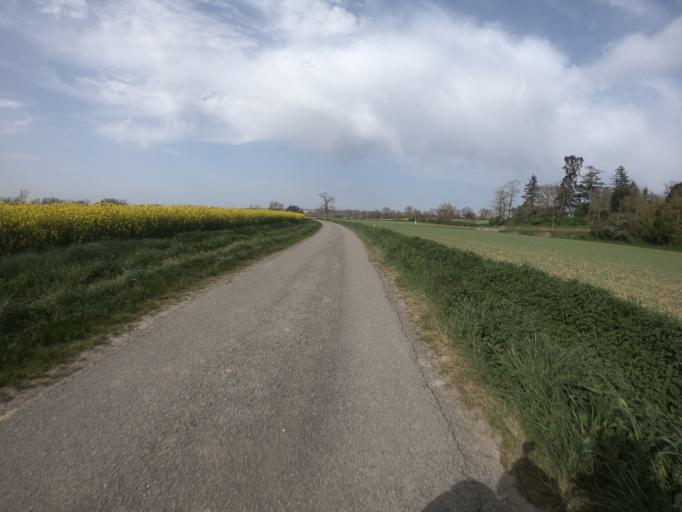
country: FR
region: Languedoc-Roussillon
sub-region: Departement de l'Aude
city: Belpech
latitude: 43.1854
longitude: 1.7397
